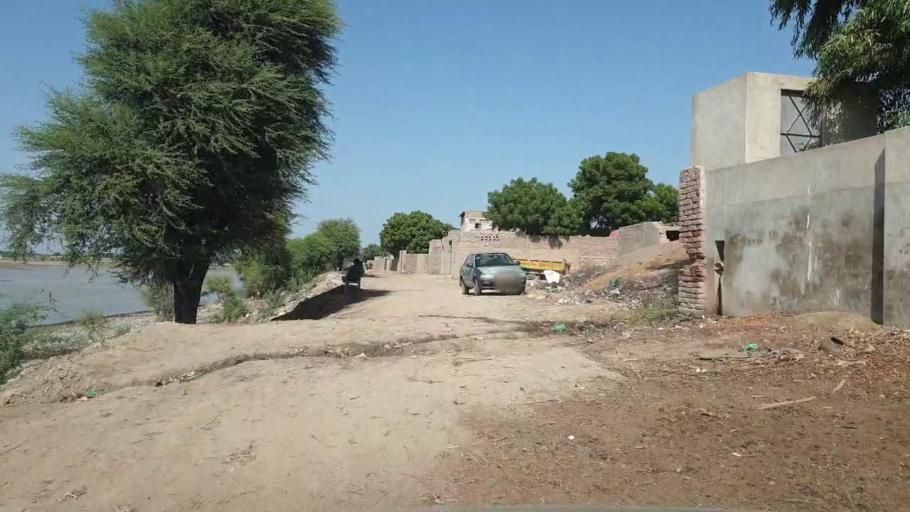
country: PK
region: Sindh
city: Matiari
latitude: 25.6500
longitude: 68.4948
